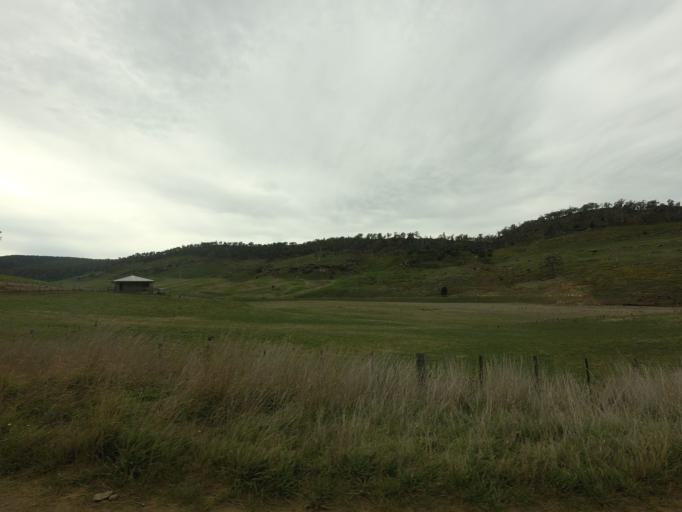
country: AU
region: Tasmania
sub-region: Derwent Valley
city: New Norfolk
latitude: -42.4048
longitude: 146.9203
